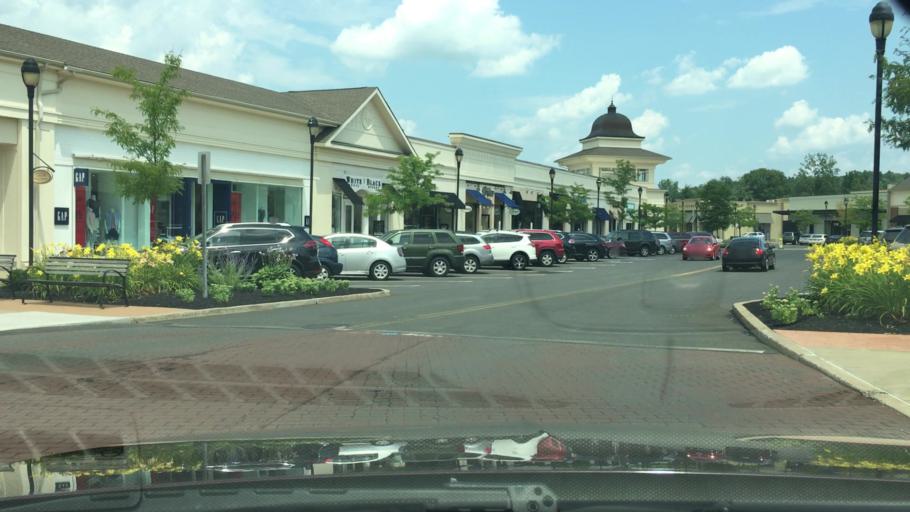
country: US
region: Connecticut
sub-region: Hartford County
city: Manchester
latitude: 41.8112
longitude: -72.5573
